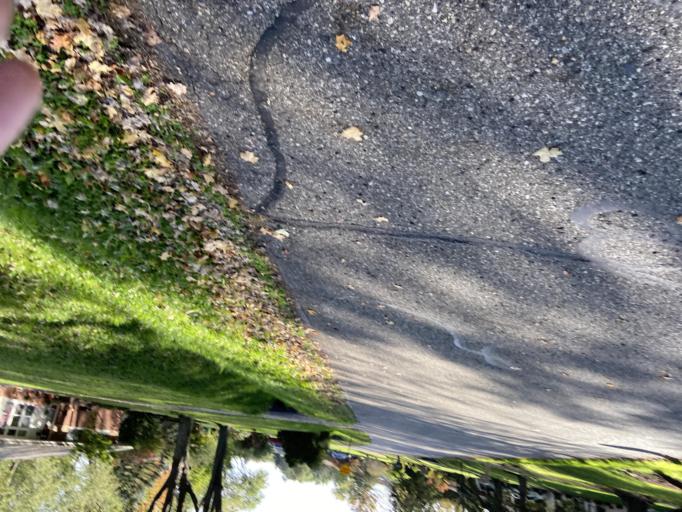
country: US
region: Michigan
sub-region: Oakland County
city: Farmington Hills
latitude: 42.5017
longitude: -83.3732
